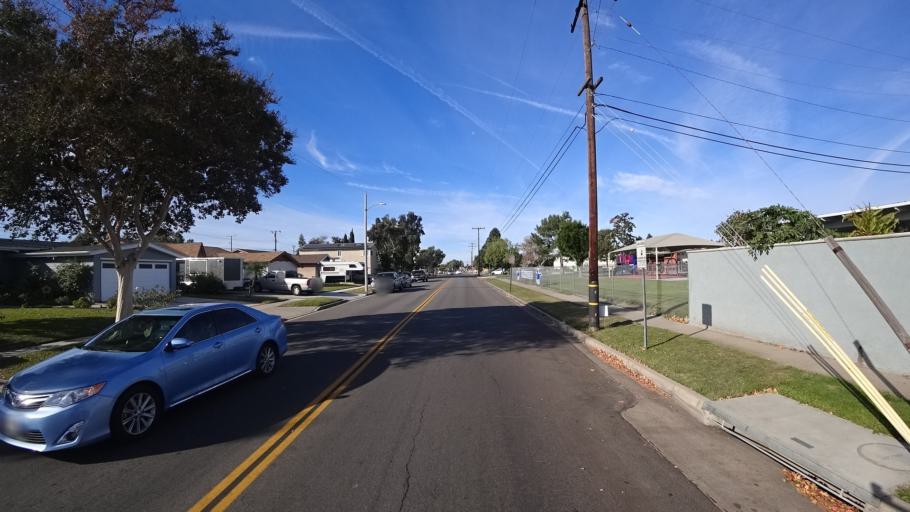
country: US
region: California
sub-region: Orange County
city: Garden Grove
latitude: 33.7564
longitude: -117.9445
